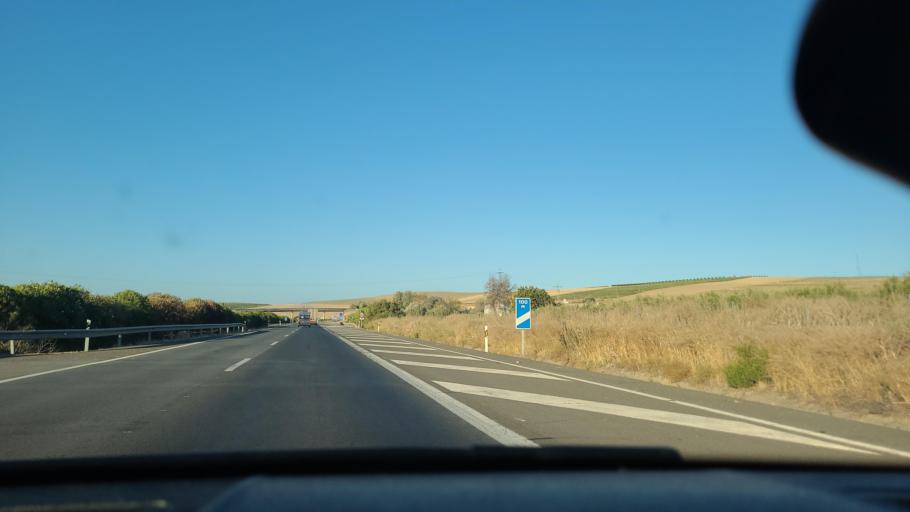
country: ES
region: Andalusia
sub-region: Province of Cordoba
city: Villafranca de Cordoba
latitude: 37.9157
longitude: -4.5919
